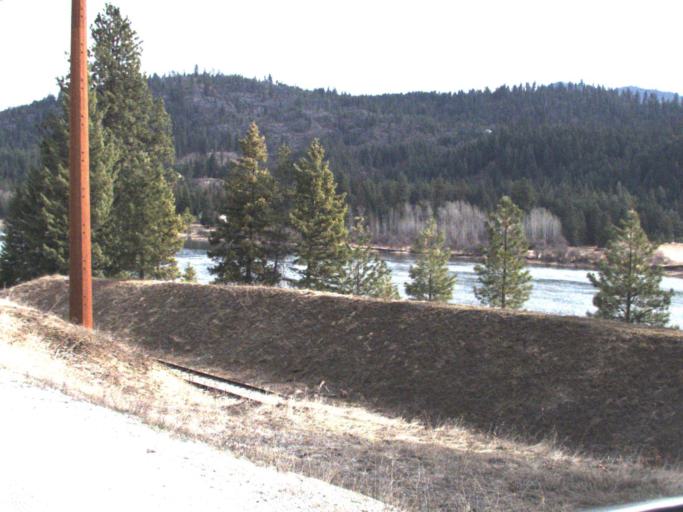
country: US
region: Washington
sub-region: Pend Oreille County
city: Newport
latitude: 48.4954
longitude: -117.2686
